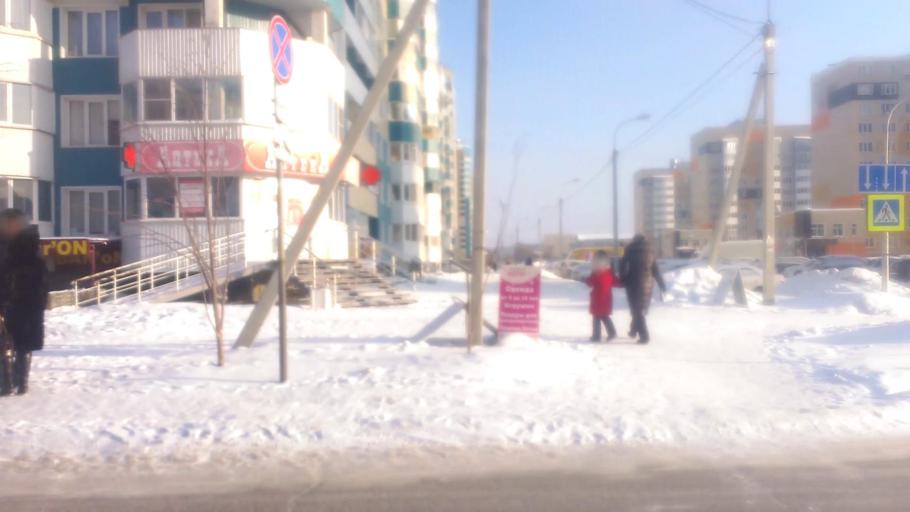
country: RU
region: Altai Krai
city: Novosilikatnyy
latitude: 53.3412
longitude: 83.6547
